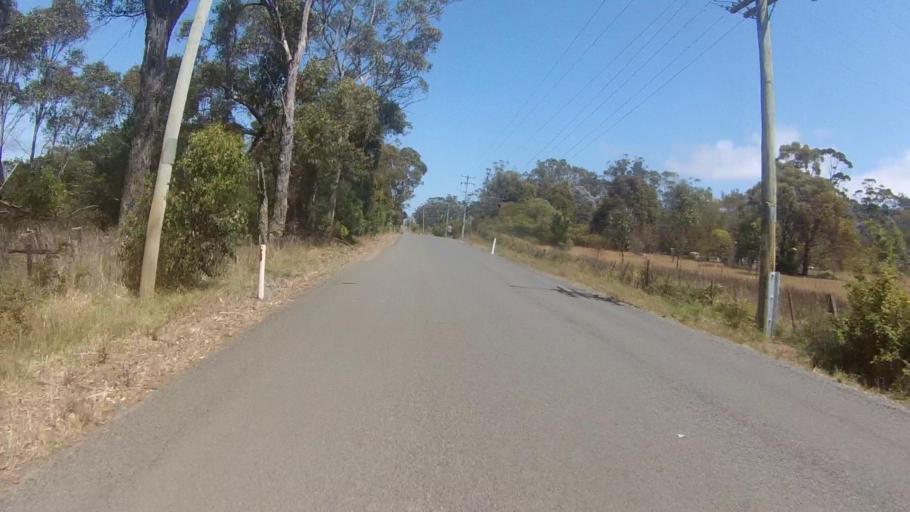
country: AU
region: Tasmania
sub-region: Sorell
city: Sorell
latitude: -42.8571
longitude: 147.8366
